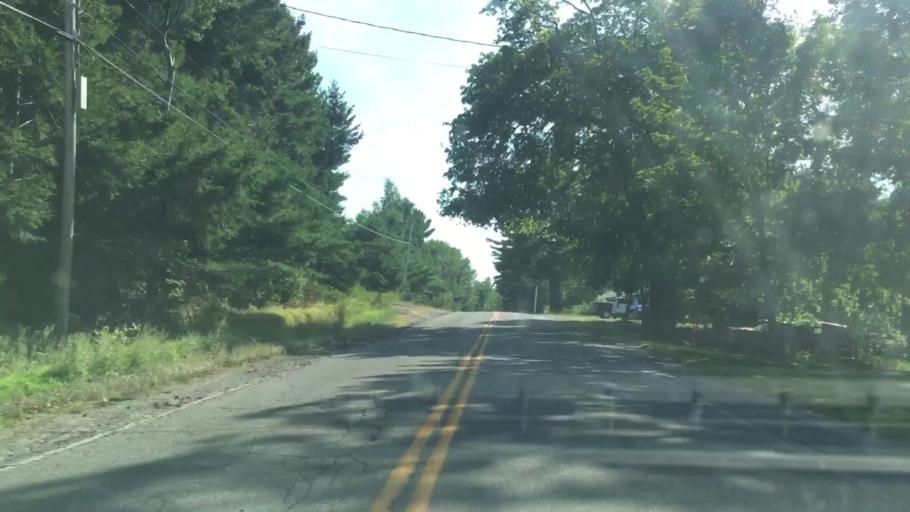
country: US
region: Maine
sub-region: Penobscot County
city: Lincoln
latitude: 45.3187
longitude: -68.5351
